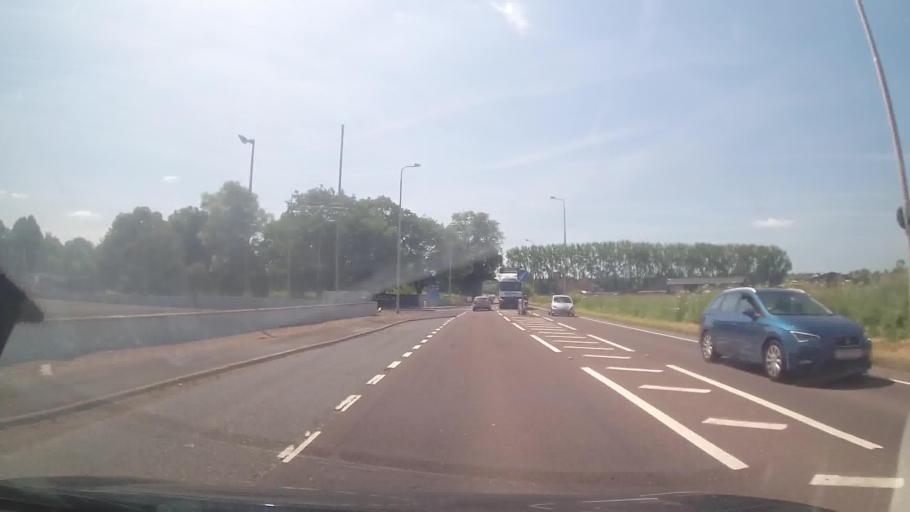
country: GB
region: England
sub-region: Herefordshire
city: Wellington
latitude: 52.1150
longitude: -2.7316
